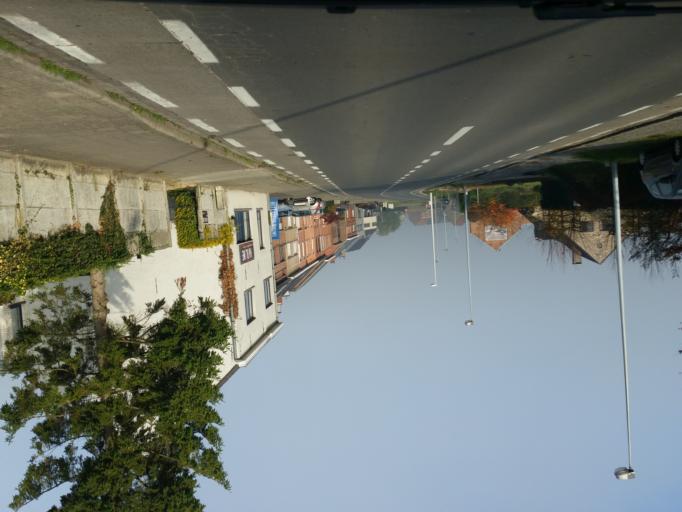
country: BE
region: Flanders
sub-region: Provincie Oost-Vlaanderen
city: Aalst
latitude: 50.9455
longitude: 4.0809
